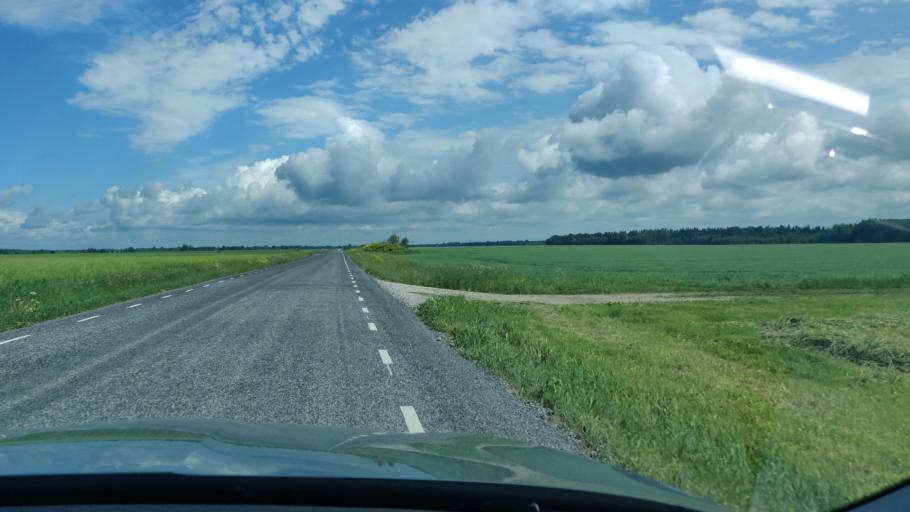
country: EE
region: Jaervamaa
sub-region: Paide linn
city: Paide
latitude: 58.8611
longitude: 25.6634
